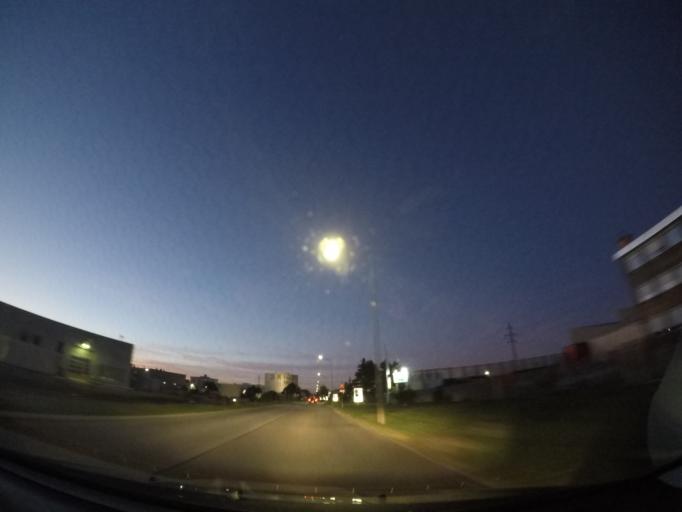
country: AT
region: Lower Austria
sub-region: Politischer Bezirk Modling
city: Biedermannsdorf
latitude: 48.0722
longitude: 16.3352
